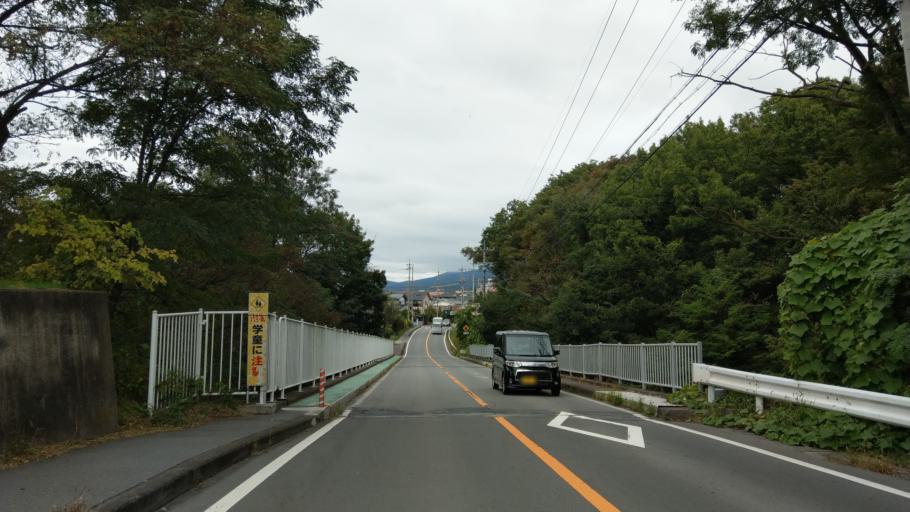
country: JP
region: Nagano
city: Komoro
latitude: 36.3186
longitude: 138.4287
